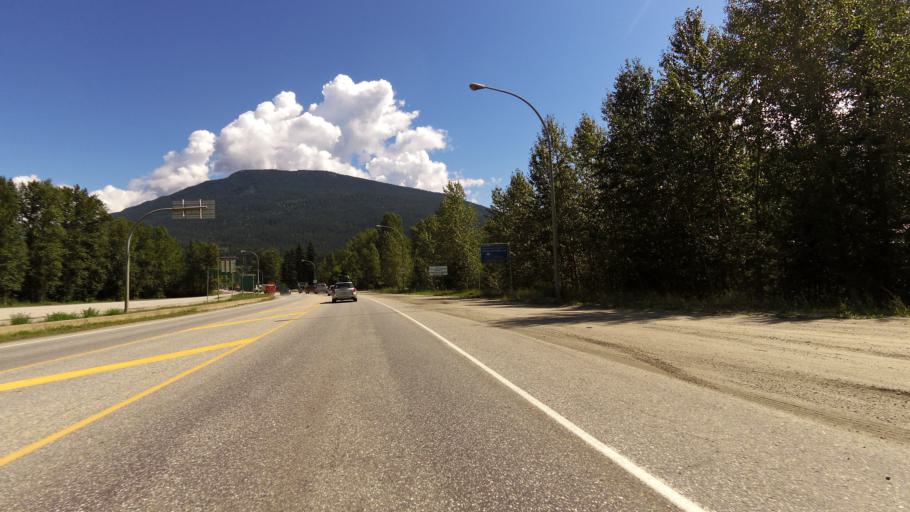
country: CA
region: British Columbia
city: Revelstoke
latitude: 51.0034
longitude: -118.2247
